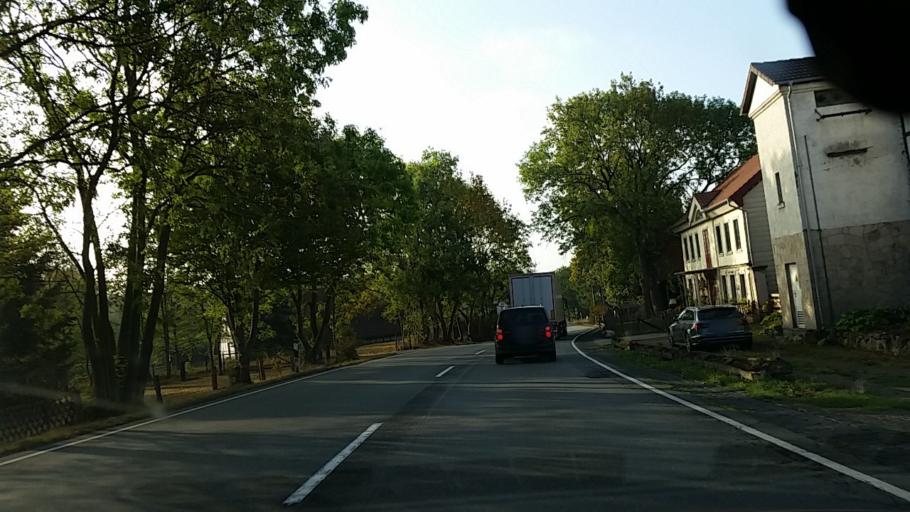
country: DE
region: Lower Saxony
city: Bad Sachsa
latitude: 51.5687
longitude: 10.5211
